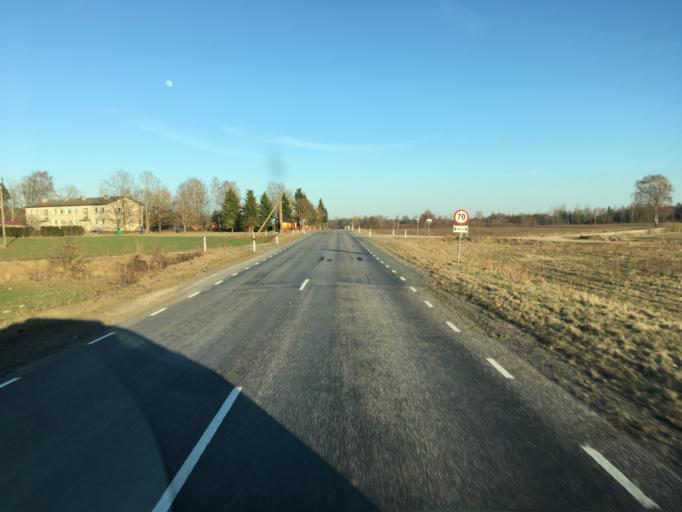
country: EE
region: Raplamaa
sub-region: Rapla vald
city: Rapla
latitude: 59.0829
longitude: 24.8232
